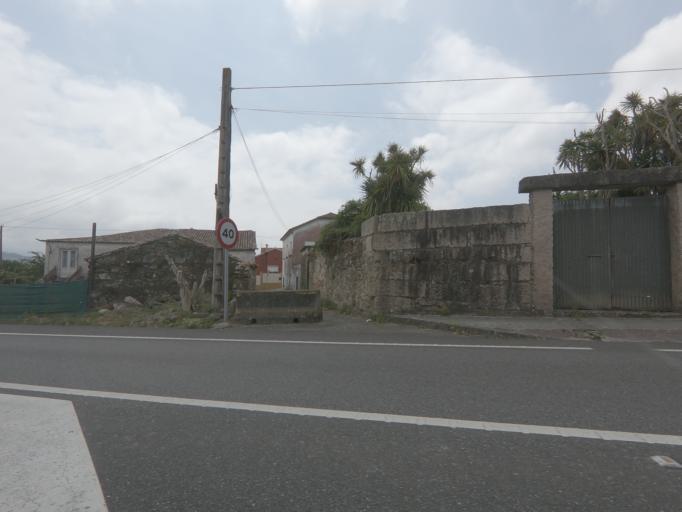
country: ES
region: Galicia
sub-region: Provincia de Pontevedra
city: O Rosal
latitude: 41.9155
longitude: -8.8312
